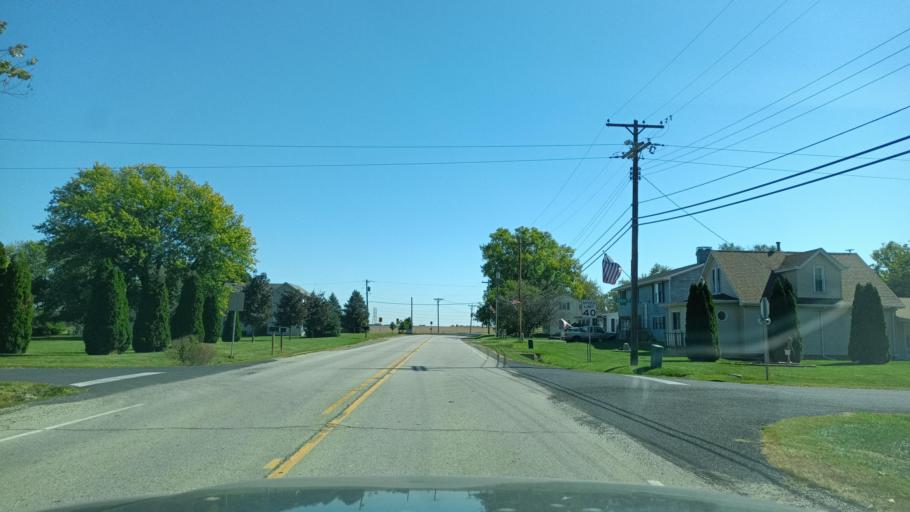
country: US
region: Illinois
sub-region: Peoria County
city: Dunlap
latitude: 40.7898
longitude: -89.7484
